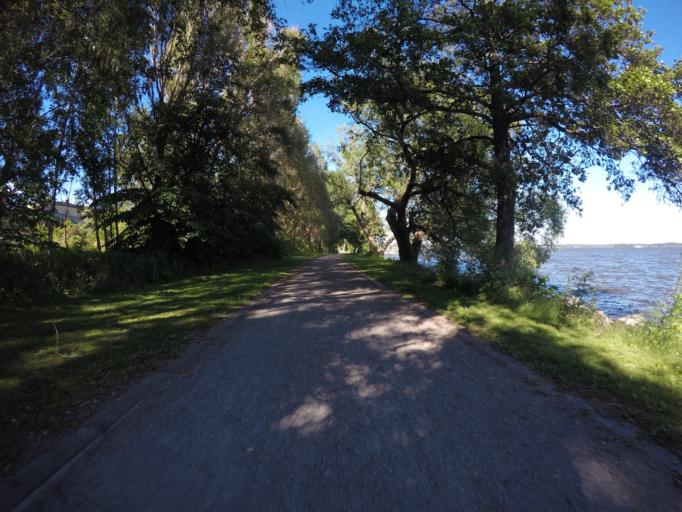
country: SE
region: Vaestmanland
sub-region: Vasteras
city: Vasteras
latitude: 59.5957
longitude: 16.5283
